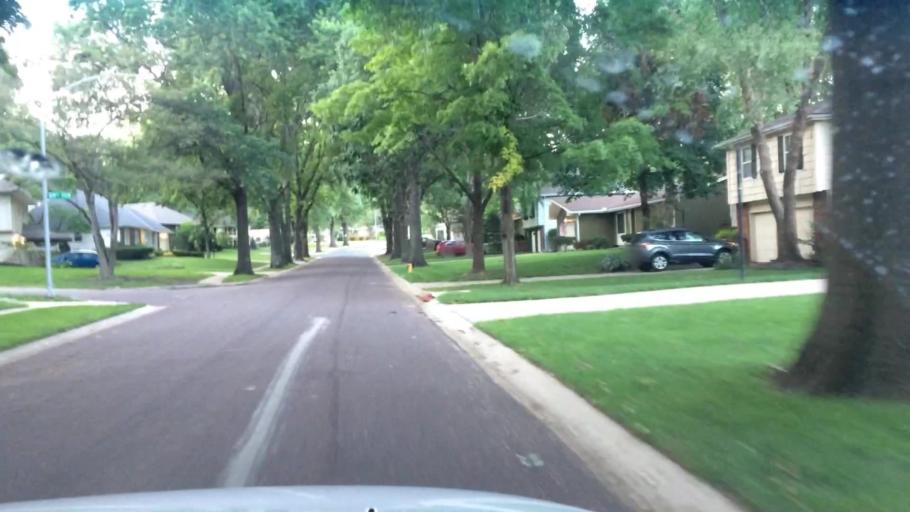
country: US
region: Kansas
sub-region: Johnson County
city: Overland Park
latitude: 38.9657
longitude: -94.6524
